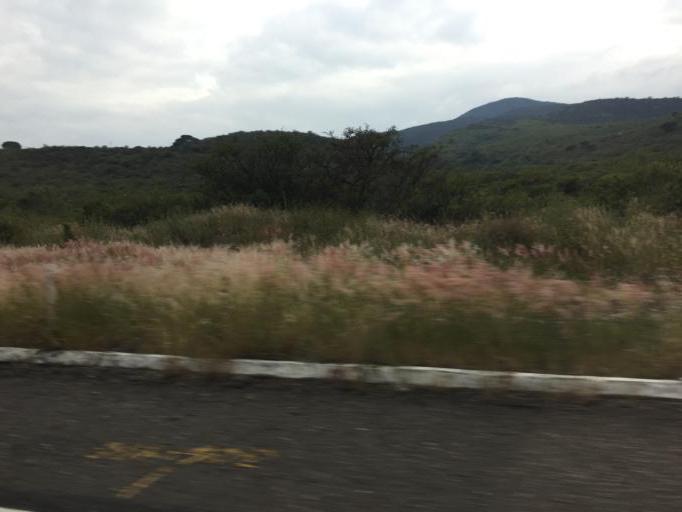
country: MX
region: Michoacan
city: Panindicuaro de la Reforma
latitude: 19.9706
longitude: -101.7191
